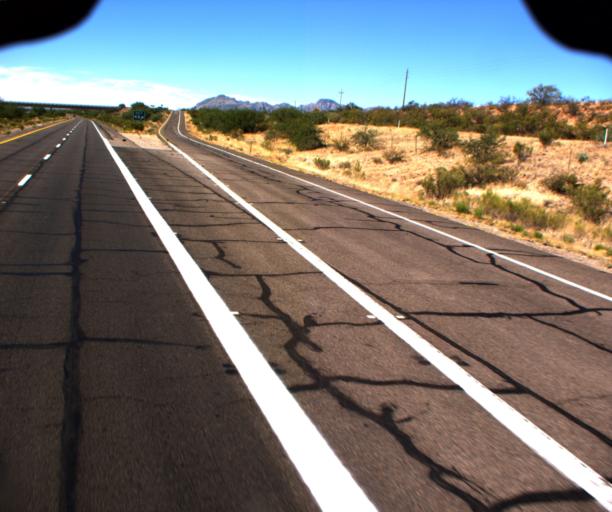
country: US
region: Arizona
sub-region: Pima County
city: Arivaca Junction
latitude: 31.6808
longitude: -111.0645
